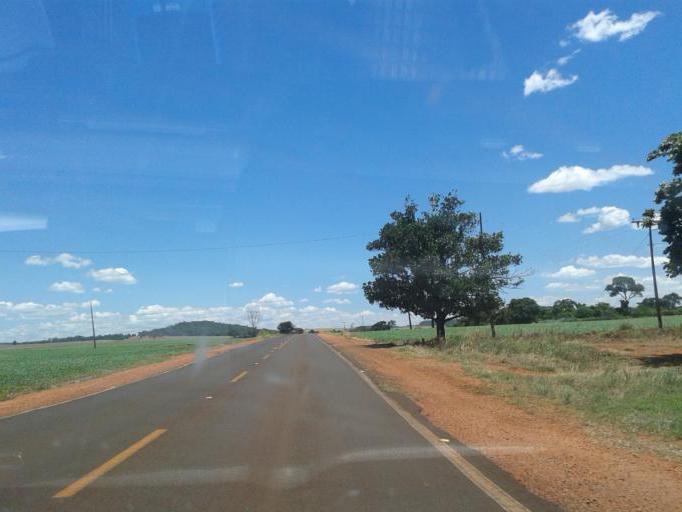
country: BR
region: Minas Gerais
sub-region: Capinopolis
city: Capinopolis
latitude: -18.5891
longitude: -49.5156
